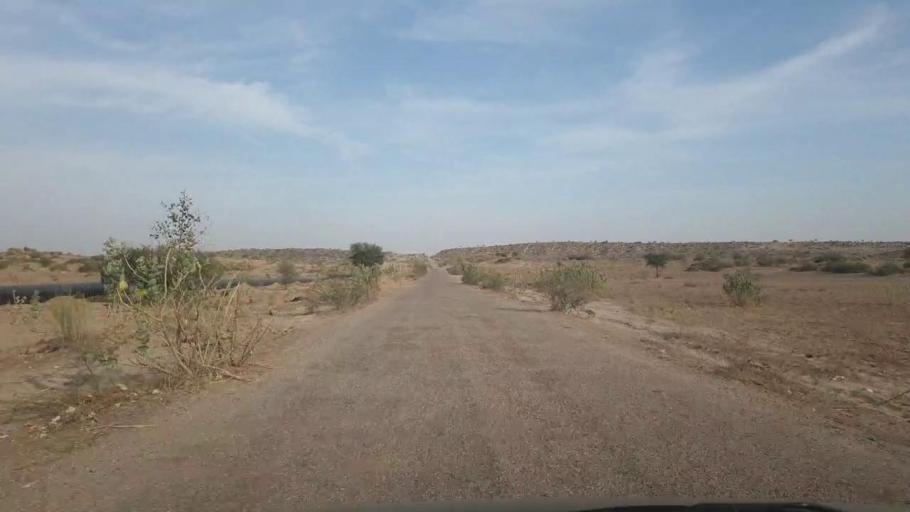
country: PK
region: Sindh
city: Nabisar
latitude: 25.0558
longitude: 69.6729
